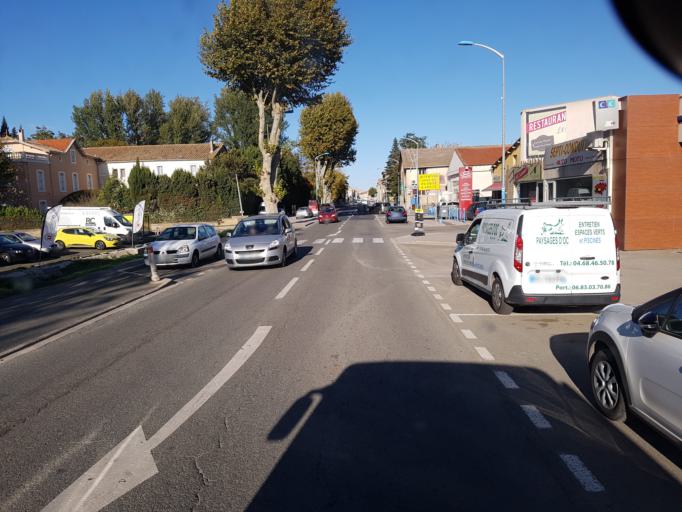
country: FR
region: Languedoc-Roussillon
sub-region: Departement de l'Aude
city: Coursan
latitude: 43.2295
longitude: 3.0519
